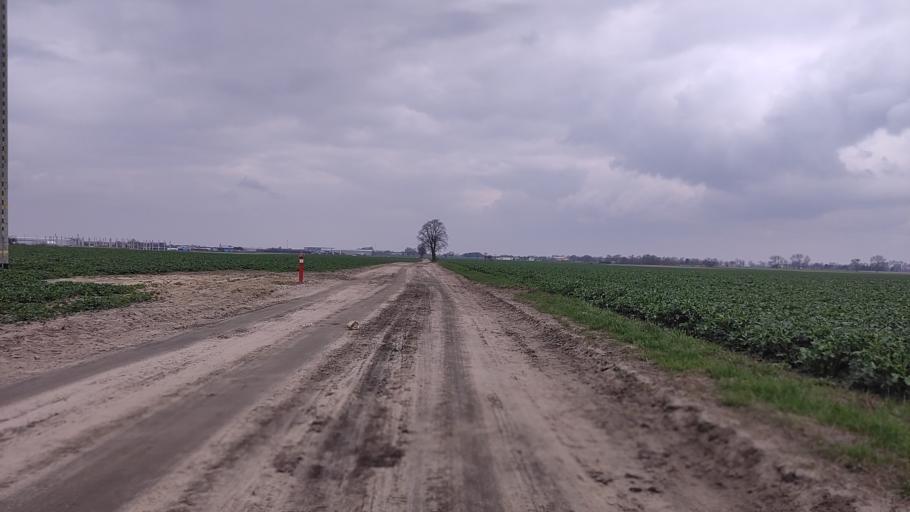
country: PL
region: Greater Poland Voivodeship
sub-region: Powiat poznanski
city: Kleszczewo
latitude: 52.4024
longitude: 17.1568
